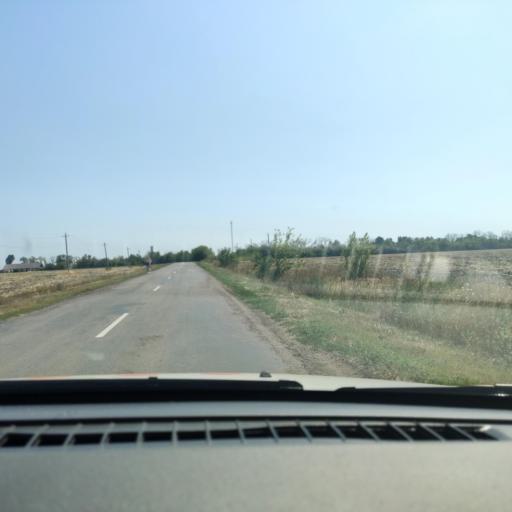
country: RU
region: Voronezj
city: Imeni Pervogo Maya
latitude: 50.7155
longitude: 39.3979
